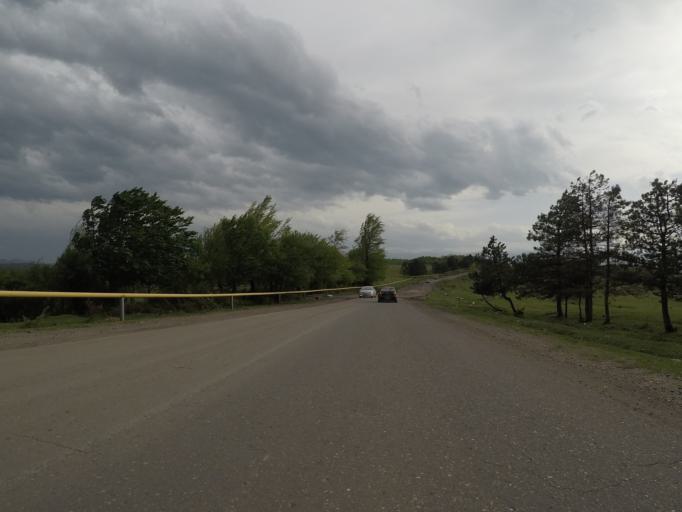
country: GE
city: Shorapani
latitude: 42.1799
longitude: 43.1357
